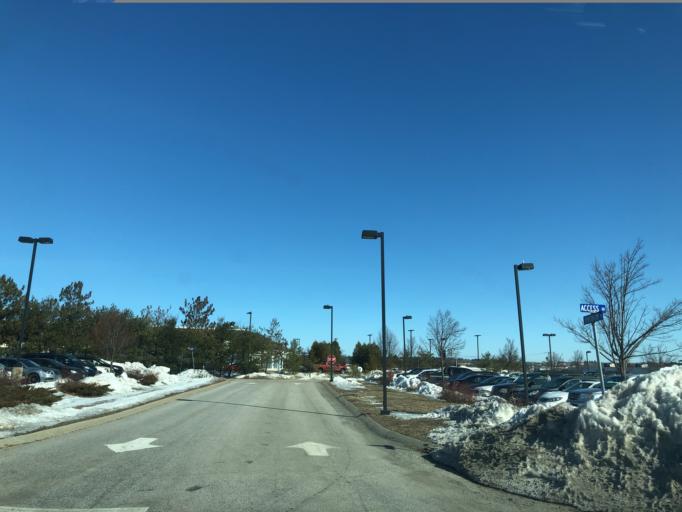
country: US
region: Maine
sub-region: Penobscot County
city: Brewer
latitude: 44.8266
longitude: -68.7449
